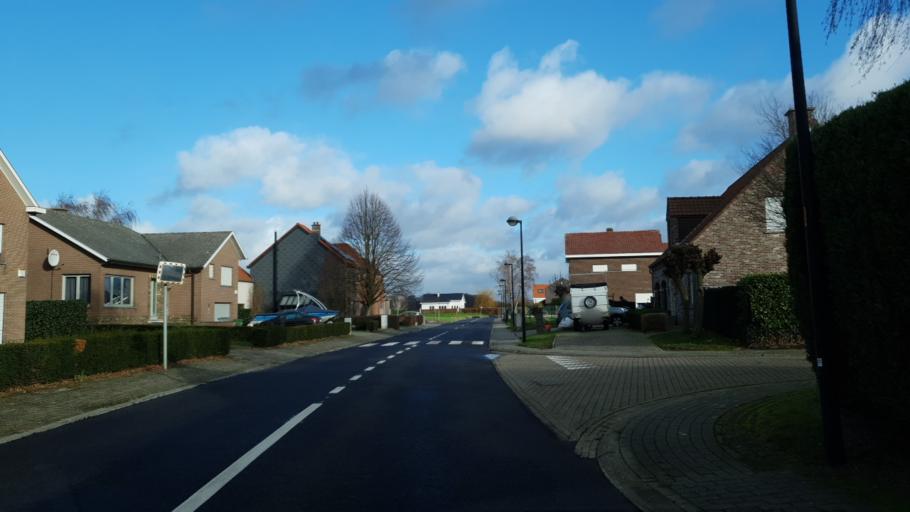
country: BE
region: Flanders
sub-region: Provincie Vlaams-Brabant
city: Kortenberg
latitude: 50.8581
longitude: 4.5526
